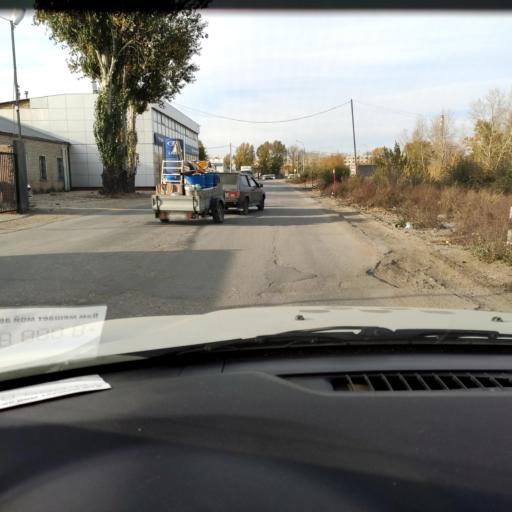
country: RU
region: Samara
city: Zhigulevsk
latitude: 53.4773
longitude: 49.4971
